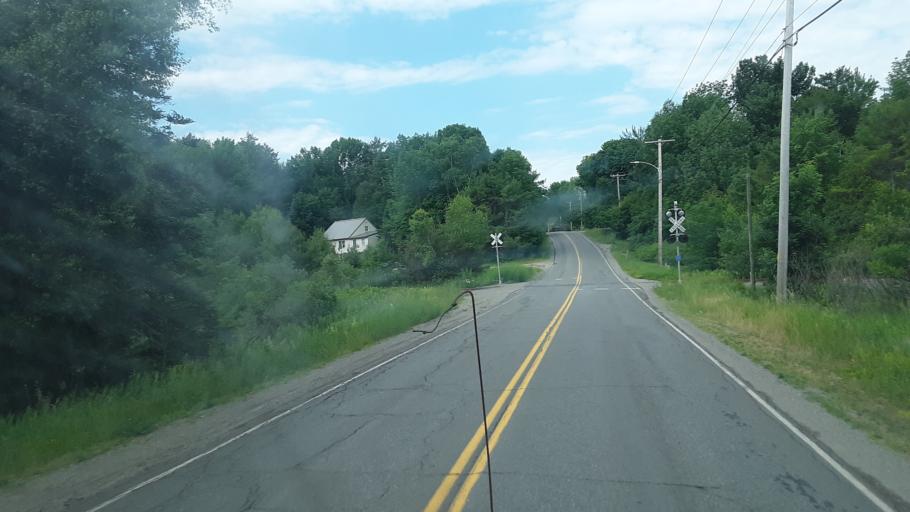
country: US
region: Maine
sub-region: Penobscot County
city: Hampden
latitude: 44.7295
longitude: -68.8702
